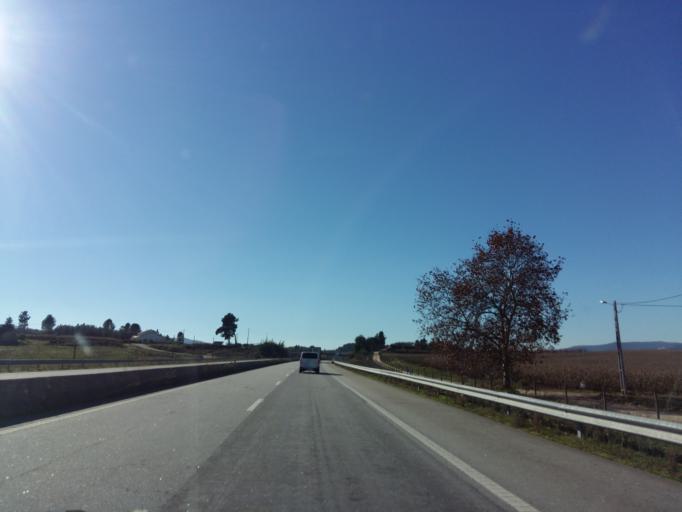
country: PT
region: Castelo Branco
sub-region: Covilha
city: Teixoso
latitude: 40.2532
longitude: -7.4498
